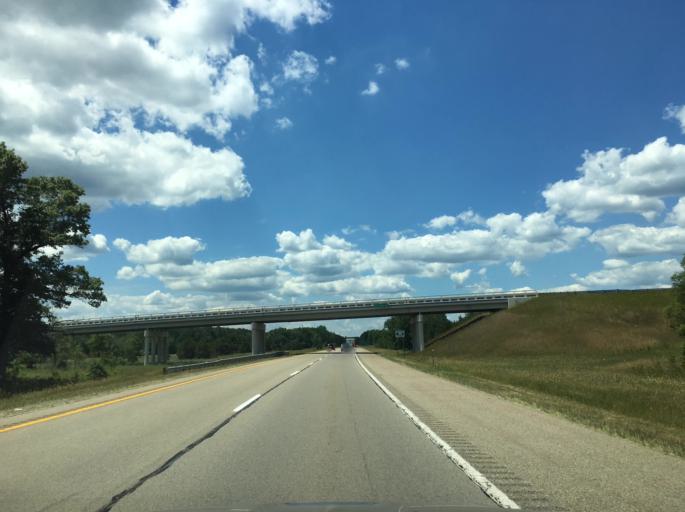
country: US
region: Michigan
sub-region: Clare County
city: Clare
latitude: 43.8740
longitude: -84.8271
